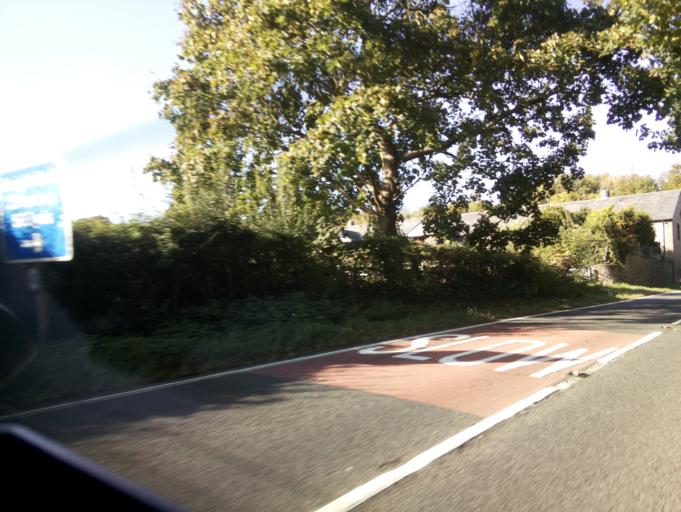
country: GB
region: England
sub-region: Hampshire
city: Swanmore
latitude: 50.9508
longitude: -1.1404
